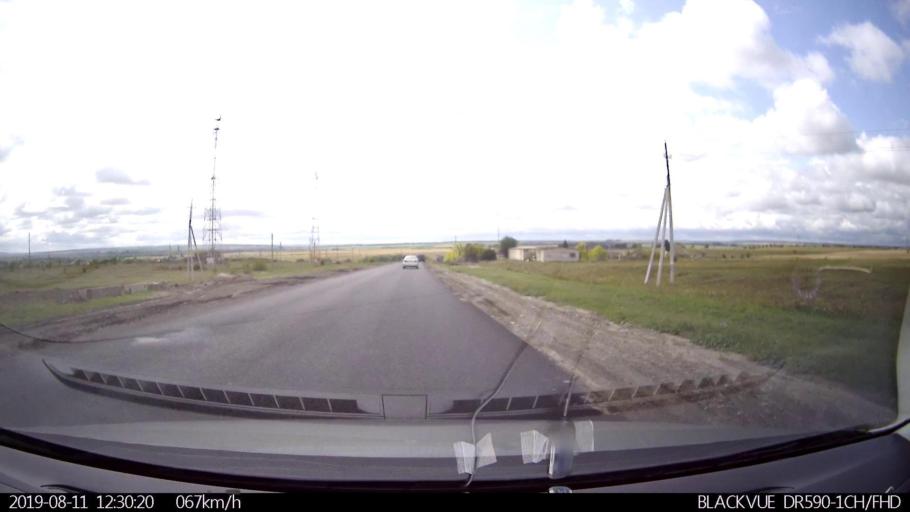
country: RU
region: Ulyanovsk
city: Ignatovka
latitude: 53.8267
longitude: 47.8950
